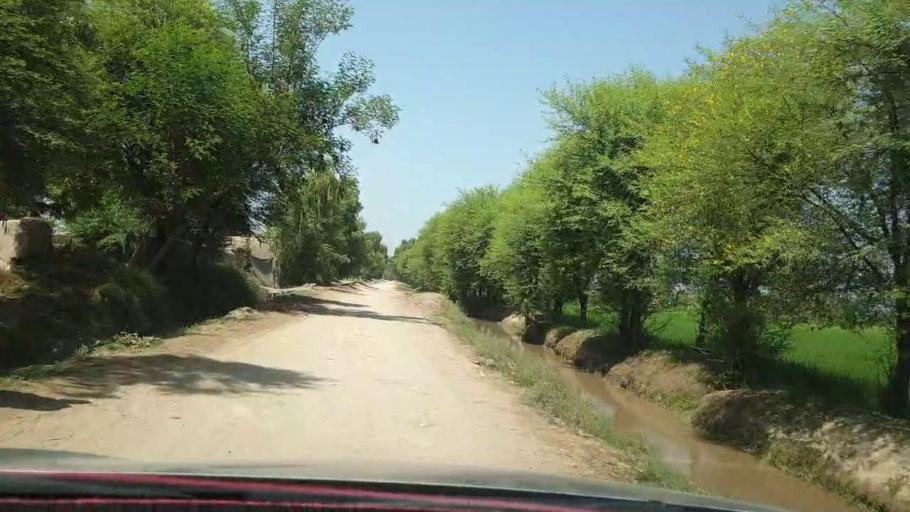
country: PK
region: Sindh
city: Warah
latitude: 27.5247
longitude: 67.8132
